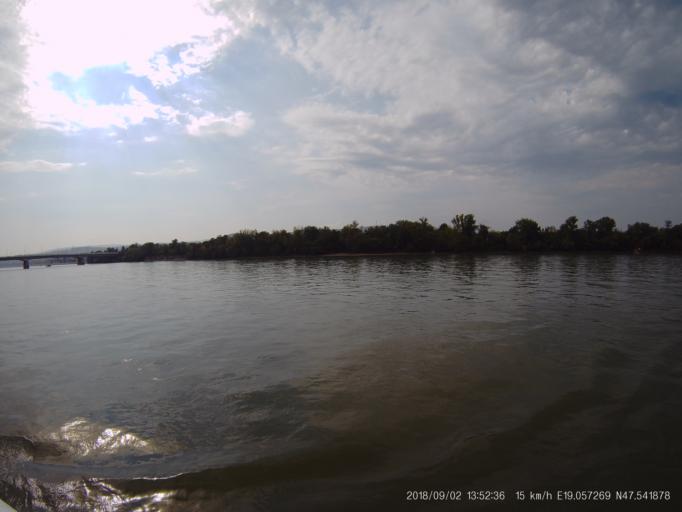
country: HU
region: Budapest
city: Budapest III. keruelet
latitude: 47.5419
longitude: 19.0573
